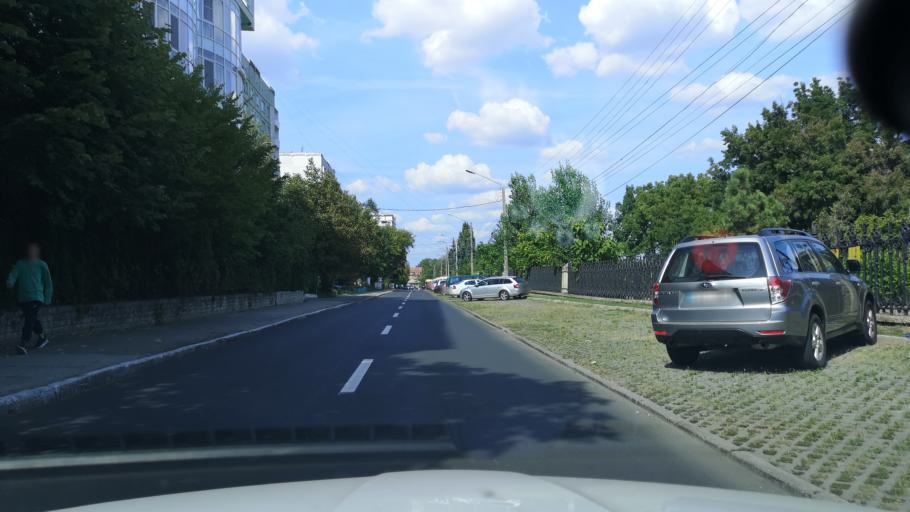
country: MD
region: Chisinau
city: Chisinau
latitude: 47.0289
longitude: 28.8081
